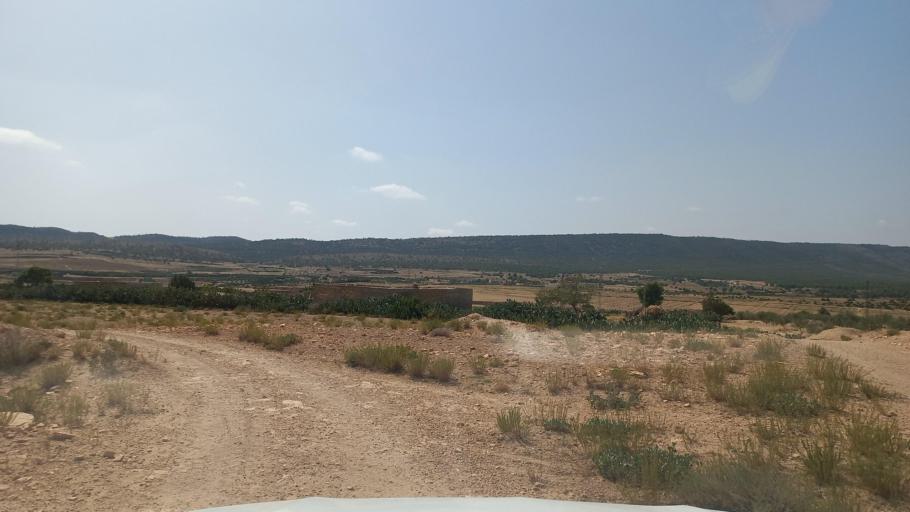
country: TN
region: Al Qasrayn
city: Sbiba
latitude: 35.3962
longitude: 8.9581
